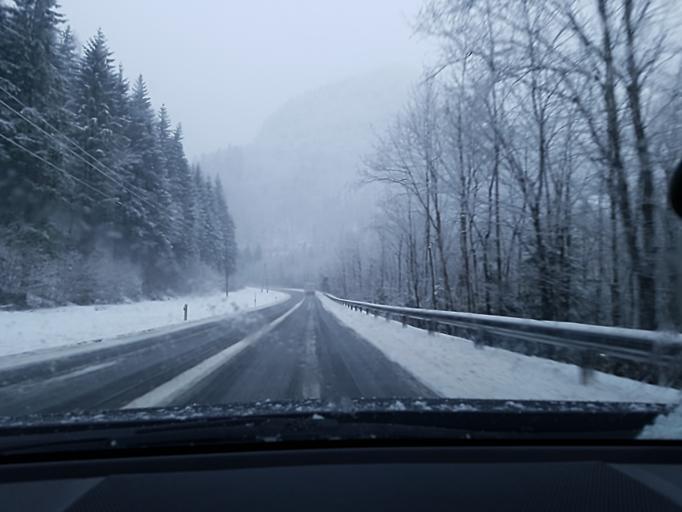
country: AT
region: Salzburg
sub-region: Politischer Bezirk Hallein
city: Scheffau am Tennengebirge
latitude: 47.5890
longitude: 13.2763
